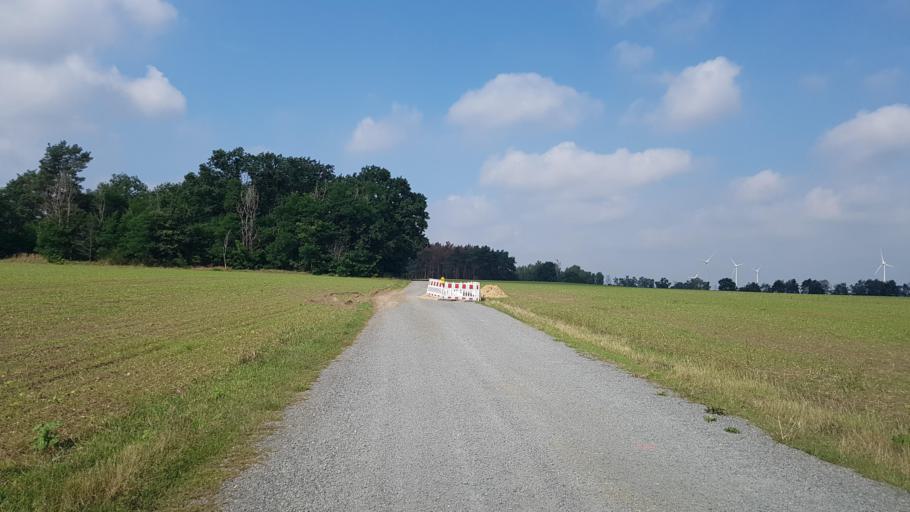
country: DE
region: Brandenburg
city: Luckau
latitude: 51.8246
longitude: 13.6830
